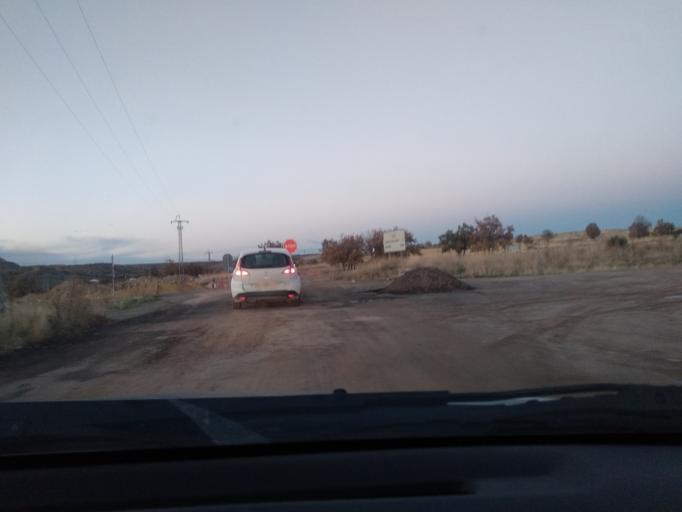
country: ES
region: Castille and Leon
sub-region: Provincia de Segovia
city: San Cristobal de Segovia
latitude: 40.9723
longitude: -4.0831
